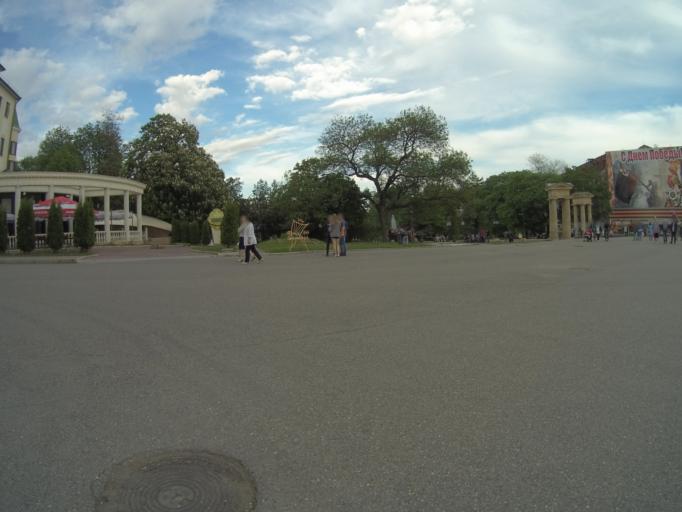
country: RU
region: Stavropol'skiy
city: Yessentuki
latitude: 44.0445
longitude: 42.8593
